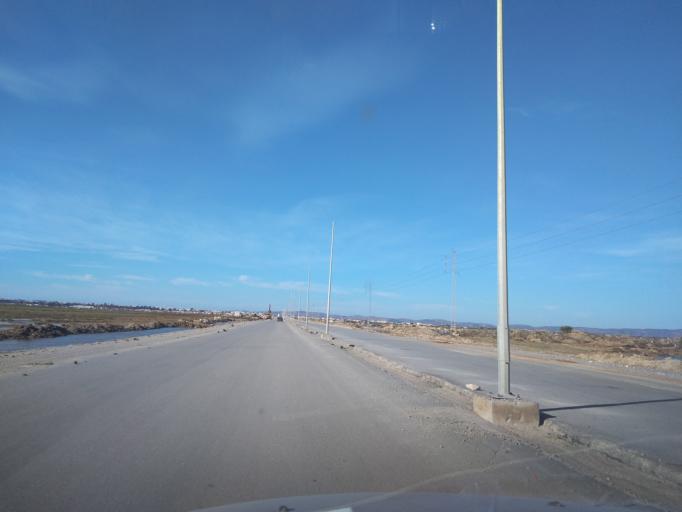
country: TN
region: Ariana
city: Qal'at al Andalus
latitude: 37.0354
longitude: 10.1340
